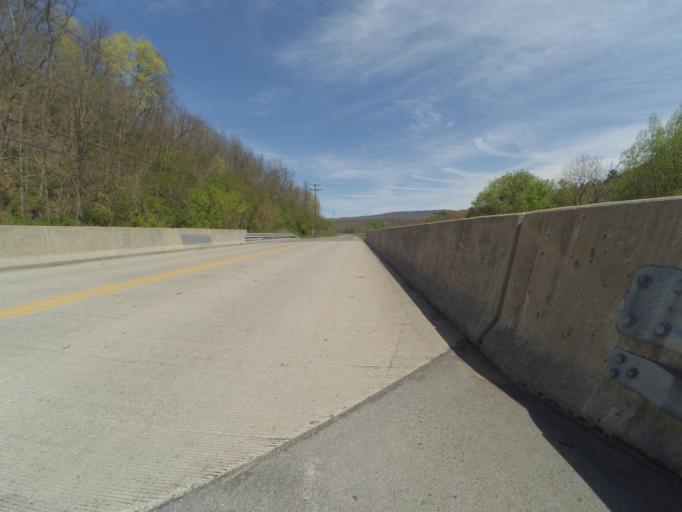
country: US
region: Pennsylvania
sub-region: Blair County
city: Tyrone
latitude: 40.6133
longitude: -78.1823
